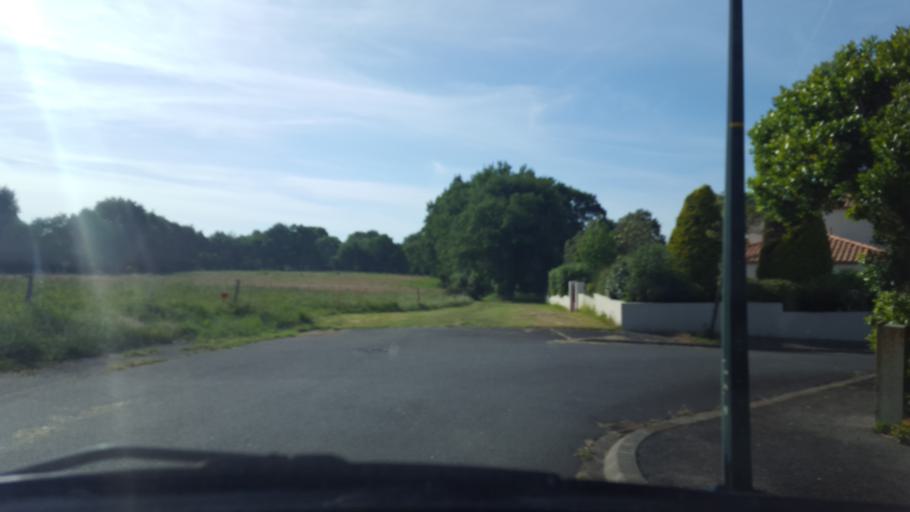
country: FR
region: Pays de la Loire
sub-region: Departement de la Loire-Atlantique
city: Saint-Philbert-de-Grand-Lieu
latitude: 47.0319
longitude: -1.6475
